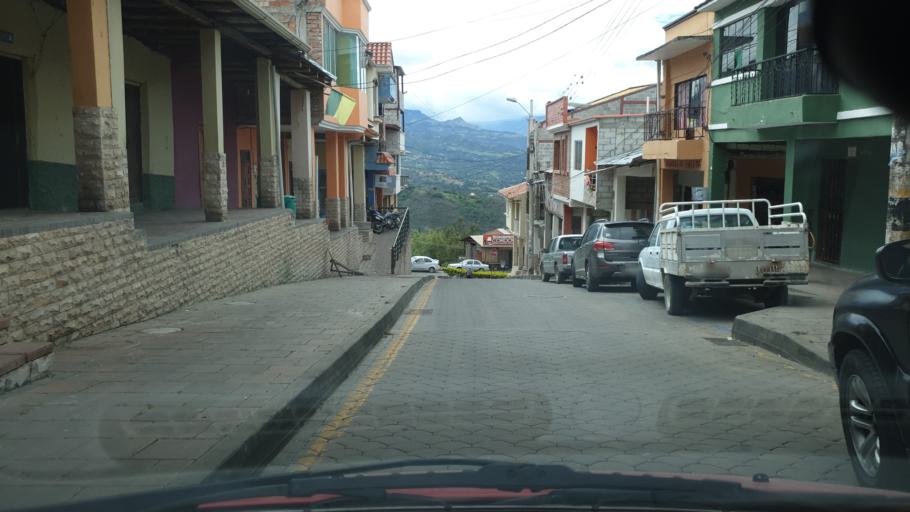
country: EC
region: Azuay
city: Cuenca
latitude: -3.2743
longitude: -79.3144
